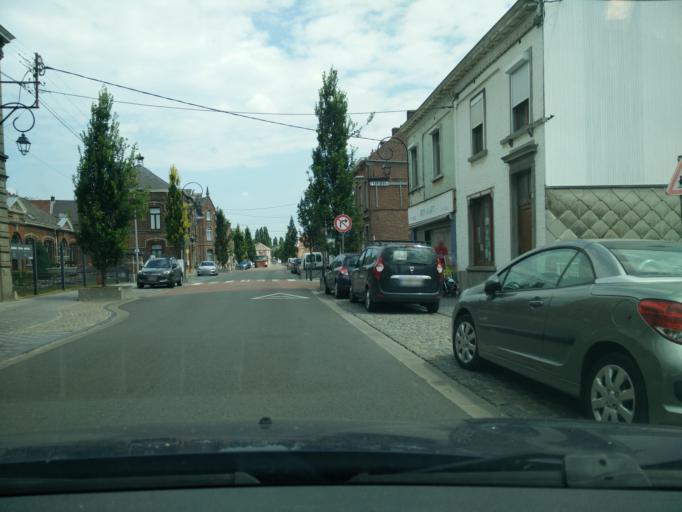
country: BE
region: Wallonia
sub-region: Province du Hainaut
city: Ecaussinnes-d'Enghien
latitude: 50.5667
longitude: 4.1659
